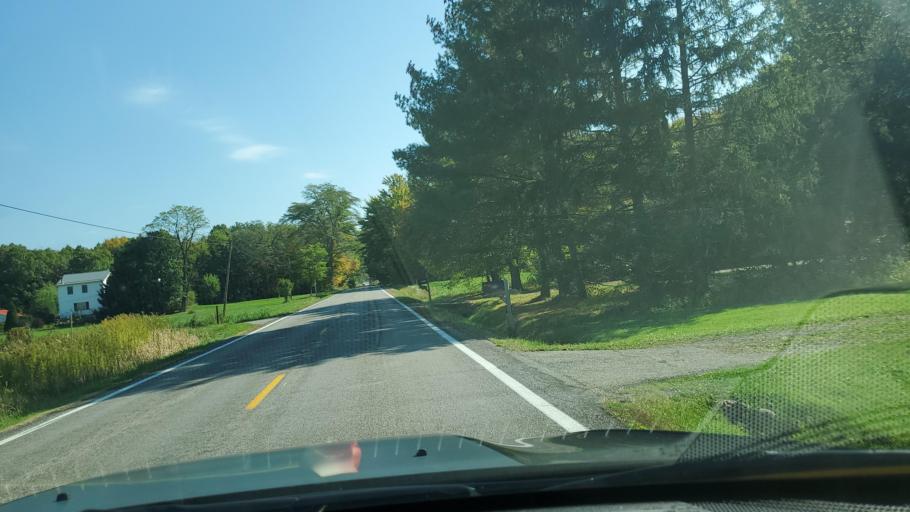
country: US
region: Ohio
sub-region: Trumbull County
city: Cortland
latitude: 41.3877
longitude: -80.6068
